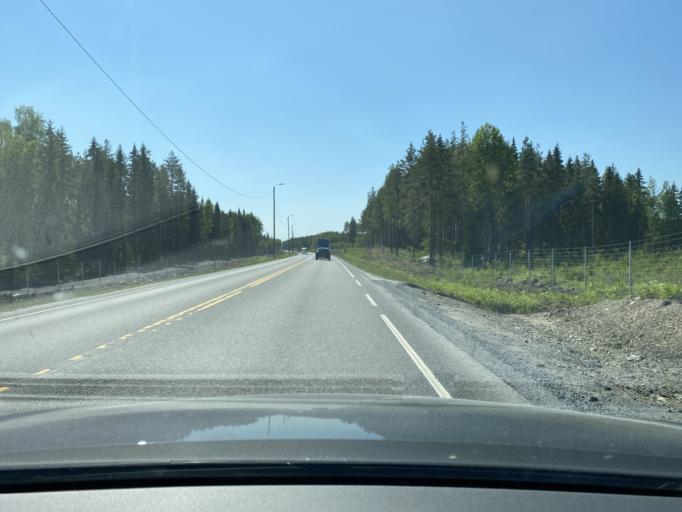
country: FI
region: Pirkanmaa
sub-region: Lounais-Pirkanmaa
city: Mouhijaervi
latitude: 61.3798
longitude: 23.1598
